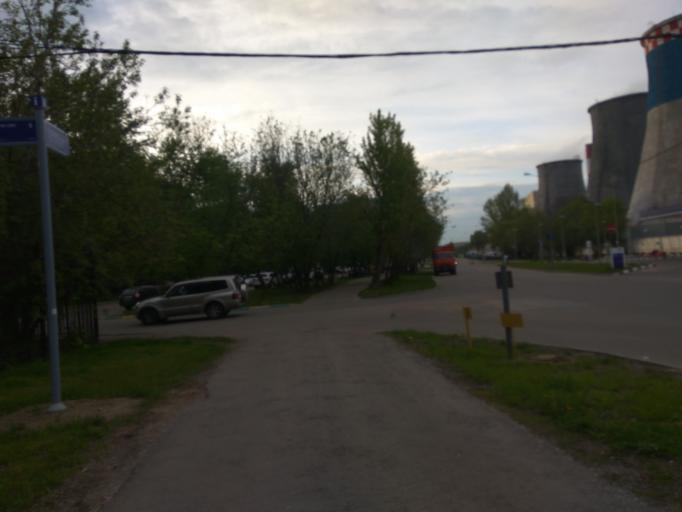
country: RU
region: Moscow
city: Sokol
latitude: 55.7783
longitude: 37.5018
